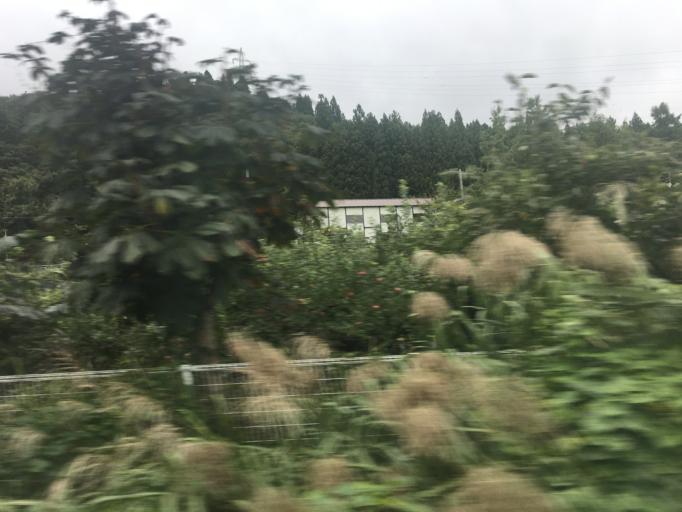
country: JP
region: Iwate
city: Shizukuishi
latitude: 39.7039
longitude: 141.0560
